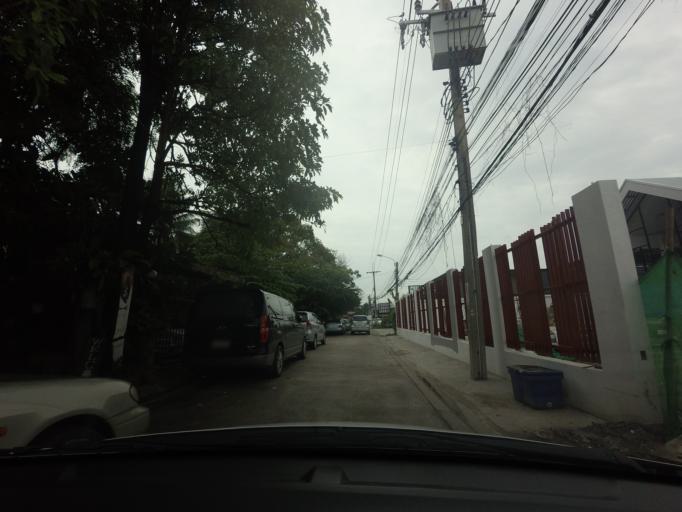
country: TH
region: Nonthaburi
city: Pak Kret
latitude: 13.9008
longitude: 100.5148
